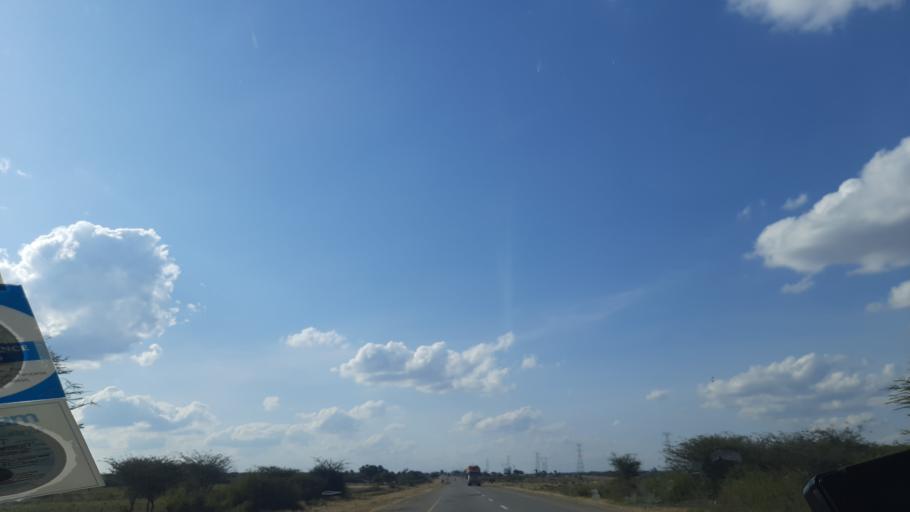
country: TZ
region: Singida
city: Ikungi
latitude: -5.1841
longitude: 34.7824
